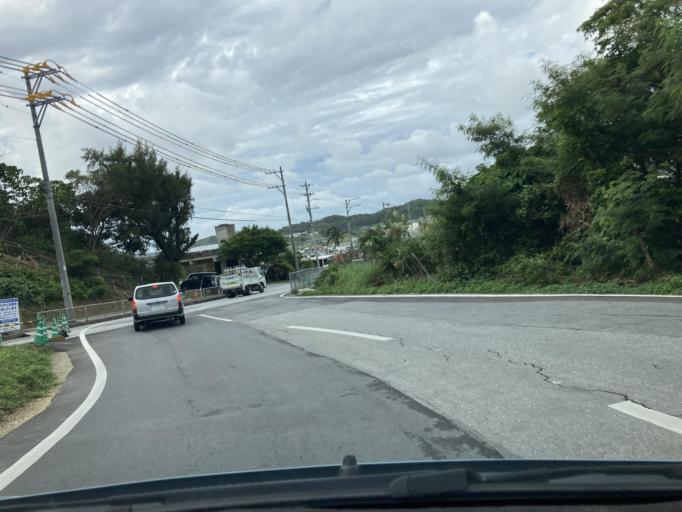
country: JP
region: Okinawa
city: Tomigusuku
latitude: 26.1791
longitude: 127.7438
